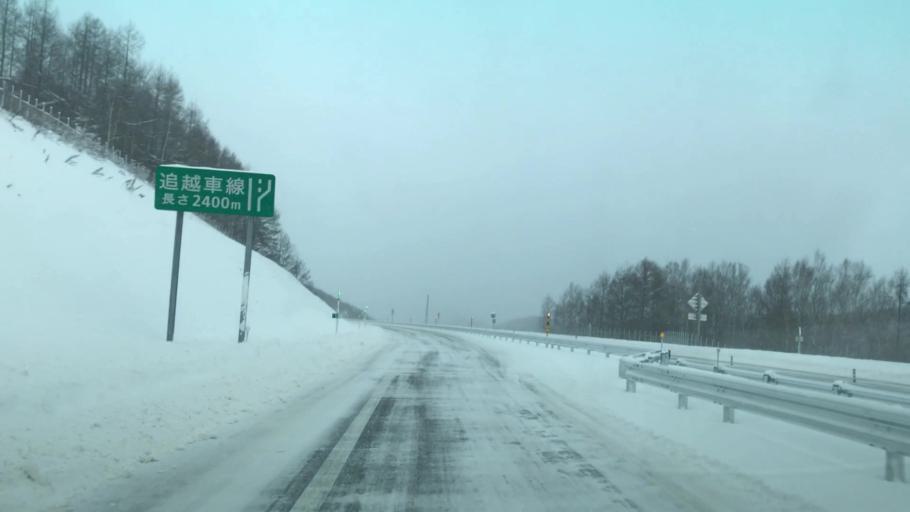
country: JP
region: Hokkaido
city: Otaru
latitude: 43.1988
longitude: 140.9455
